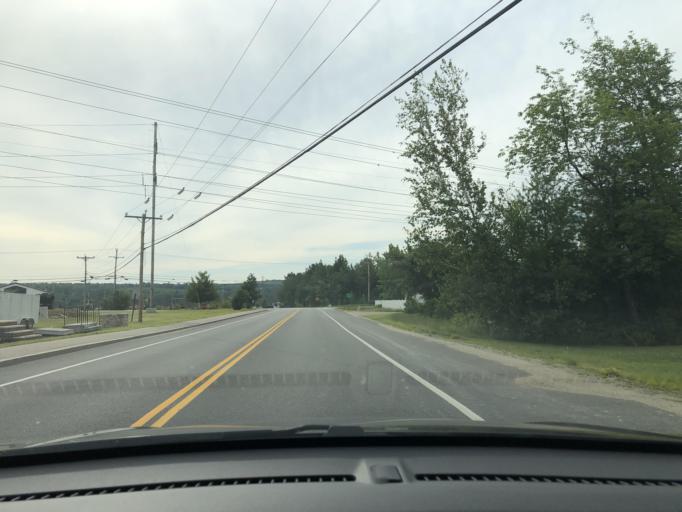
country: US
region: New Hampshire
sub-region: Merrimack County
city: Concord
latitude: 43.2087
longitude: -71.4866
